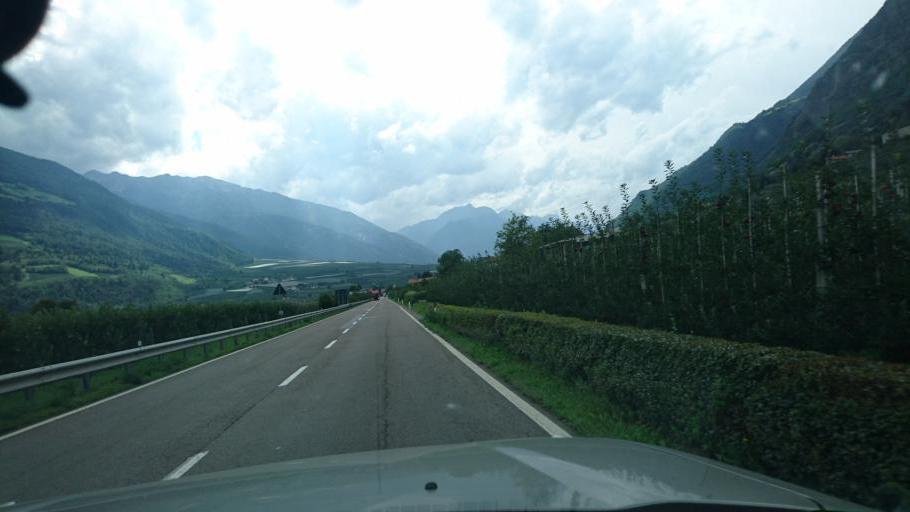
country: IT
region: Trentino-Alto Adige
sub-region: Bolzano
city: Castelbello
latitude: 46.6336
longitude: 10.9225
